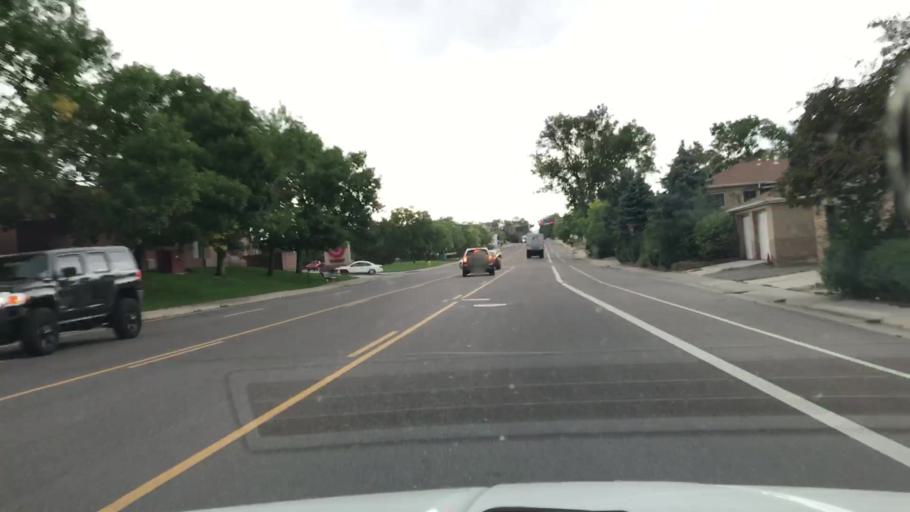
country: US
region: Colorado
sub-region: Jefferson County
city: Edgewater
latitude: 39.7477
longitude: -105.0546
